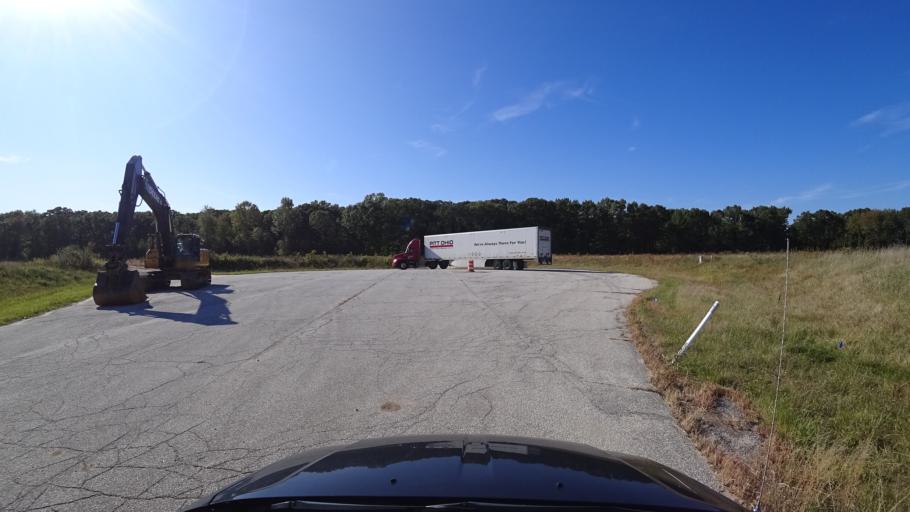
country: US
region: Indiana
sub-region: LaPorte County
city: Trail Creek
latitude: 41.6964
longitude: -86.8433
